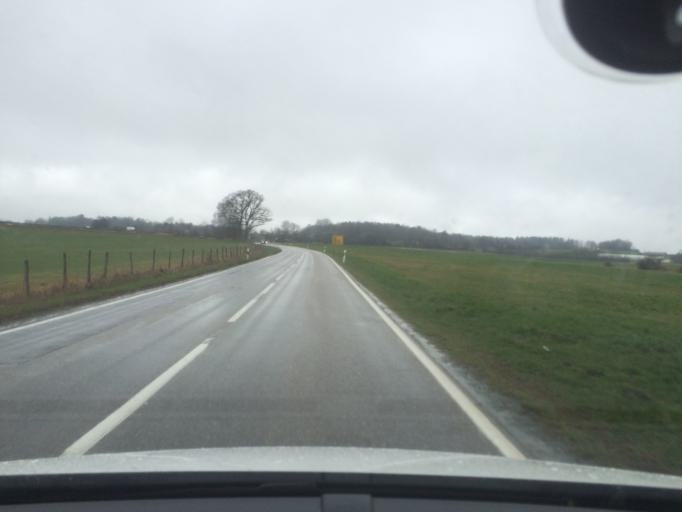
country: DE
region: Bavaria
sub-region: Upper Bavaria
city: Glonn
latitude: 47.9862
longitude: 11.9019
